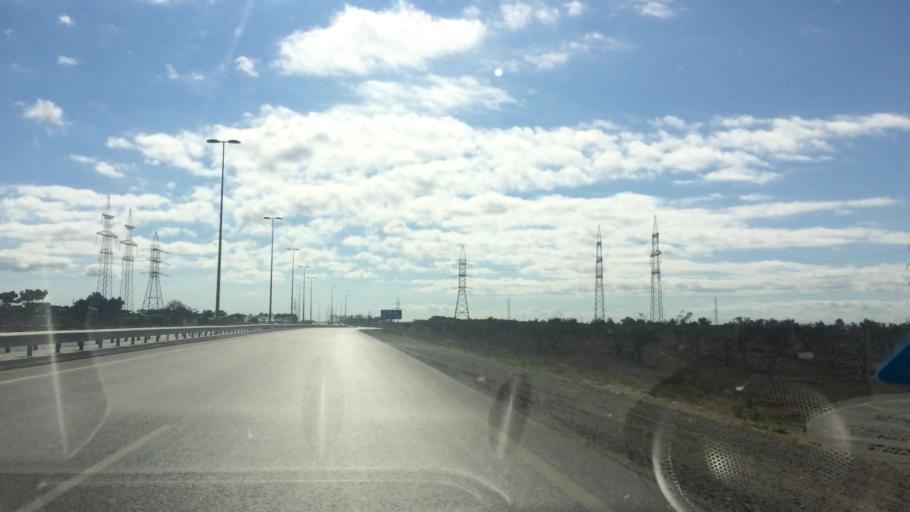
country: AZ
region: Baki
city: Qala
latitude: 40.4389
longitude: 50.1826
